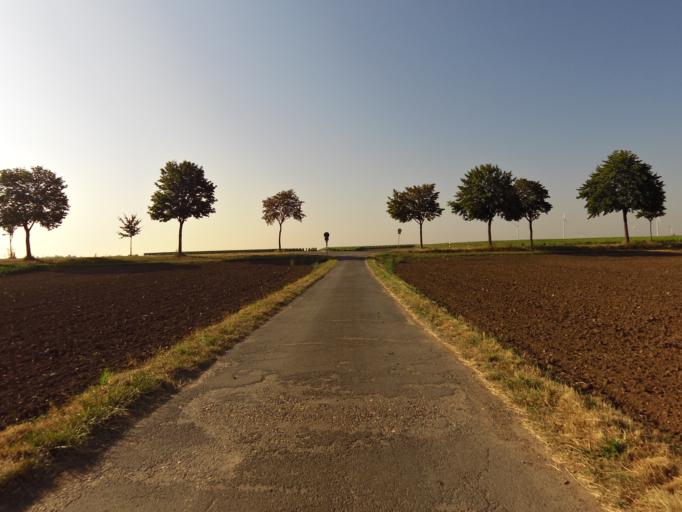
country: DE
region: Rheinland-Pfalz
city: Kleinniedesheim
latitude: 49.6051
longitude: 8.3158
